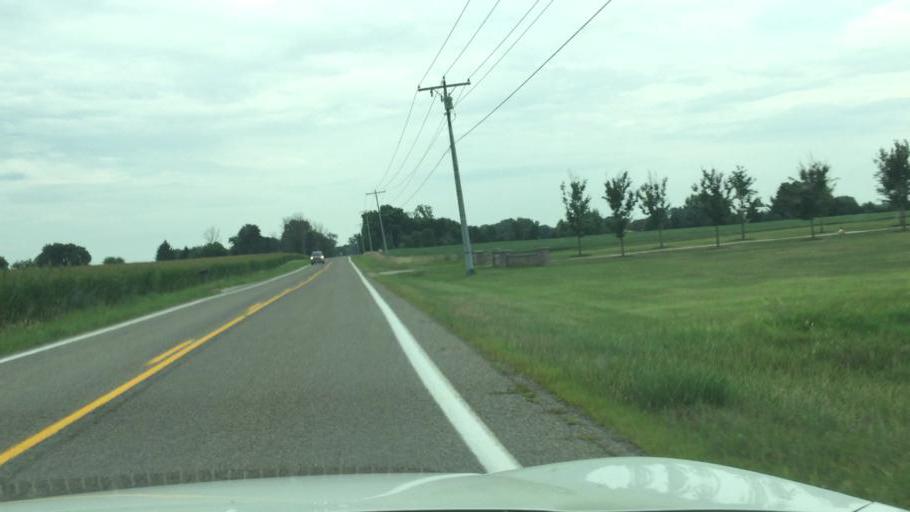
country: US
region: Ohio
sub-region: Champaign County
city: North Lewisburg
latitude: 40.2116
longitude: -83.5425
